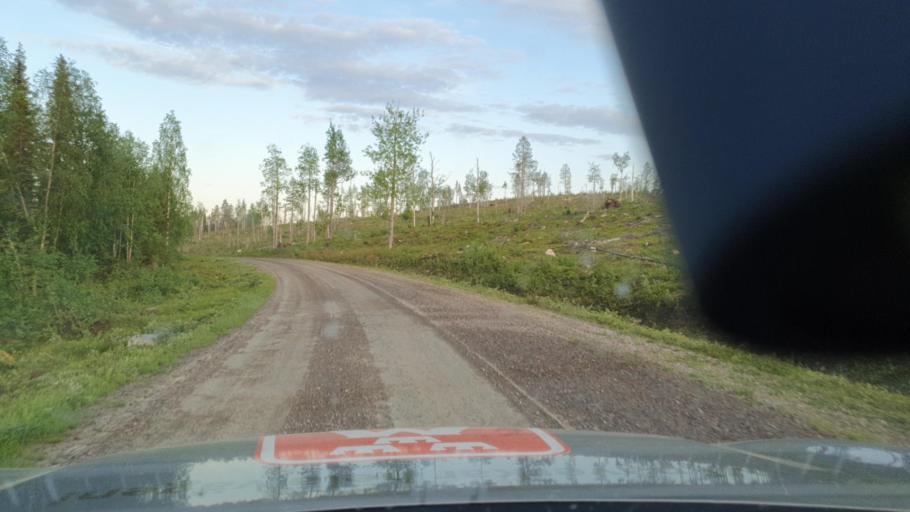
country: SE
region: Norrbotten
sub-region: Bodens Kommun
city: Boden
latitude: 66.4797
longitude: 21.6110
